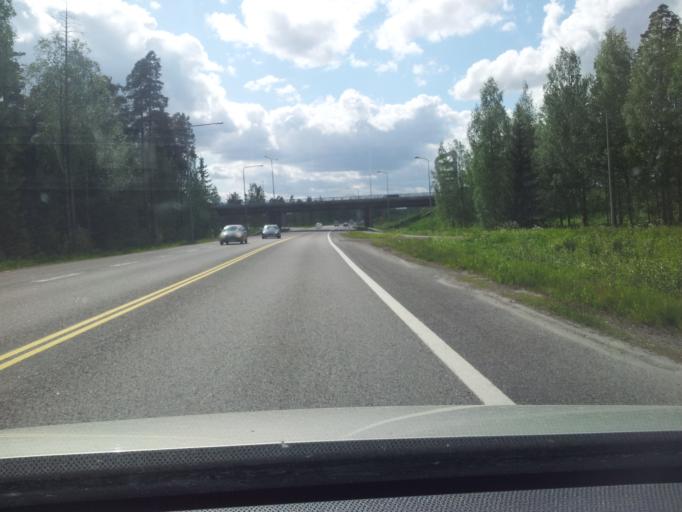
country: FI
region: Kymenlaakso
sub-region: Kouvola
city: Kouvola
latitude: 60.8753
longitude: 26.6607
